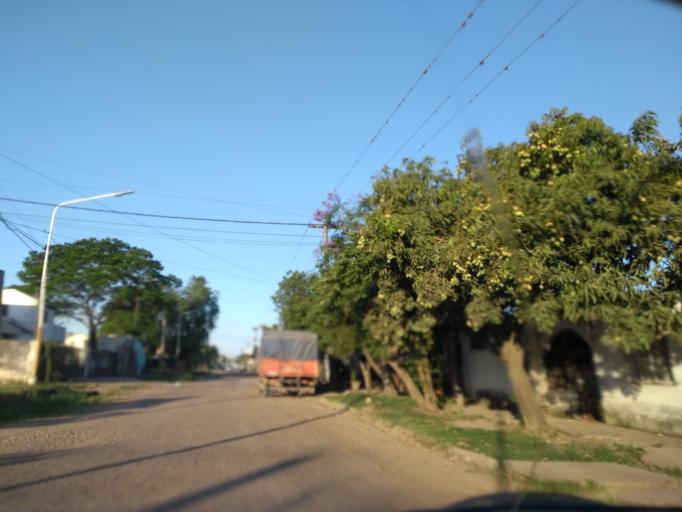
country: AR
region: Chaco
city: Barranqueras
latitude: -27.4851
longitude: -58.9387
